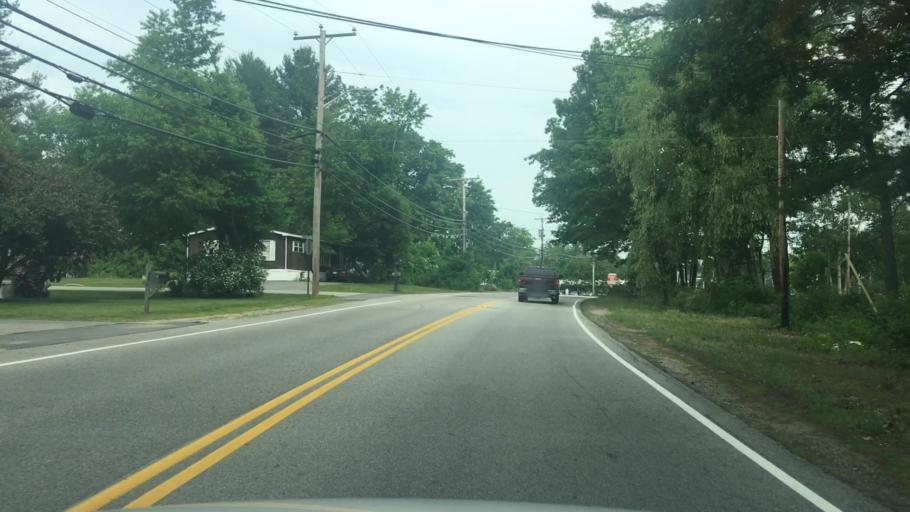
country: US
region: New Hampshire
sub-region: Rockingham County
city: Exeter
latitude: 42.9900
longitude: -70.9689
